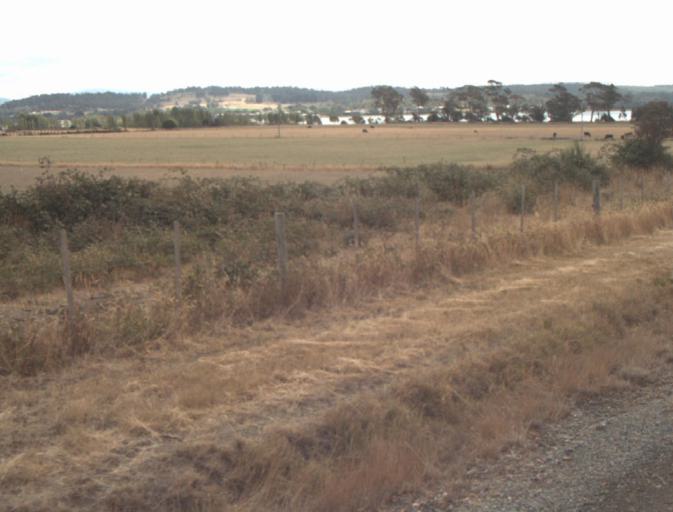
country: AU
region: Tasmania
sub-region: Launceston
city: Mayfield
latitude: -41.2893
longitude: 147.0020
